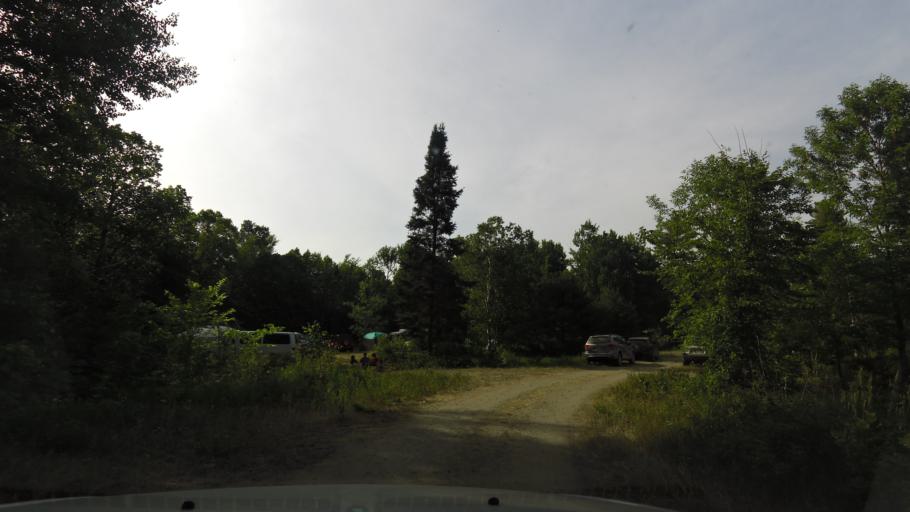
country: CA
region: Ontario
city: Greater Sudbury
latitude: 45.9088
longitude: -80.5557
